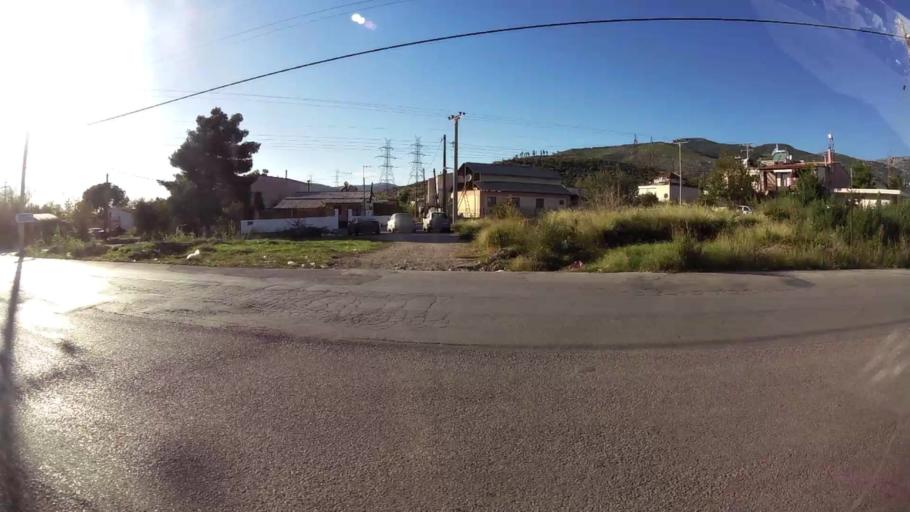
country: GR
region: Attica
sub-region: Nomarchia Anatolikis Attikis
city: Acharnes
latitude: 38.0916
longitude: 23.7206
